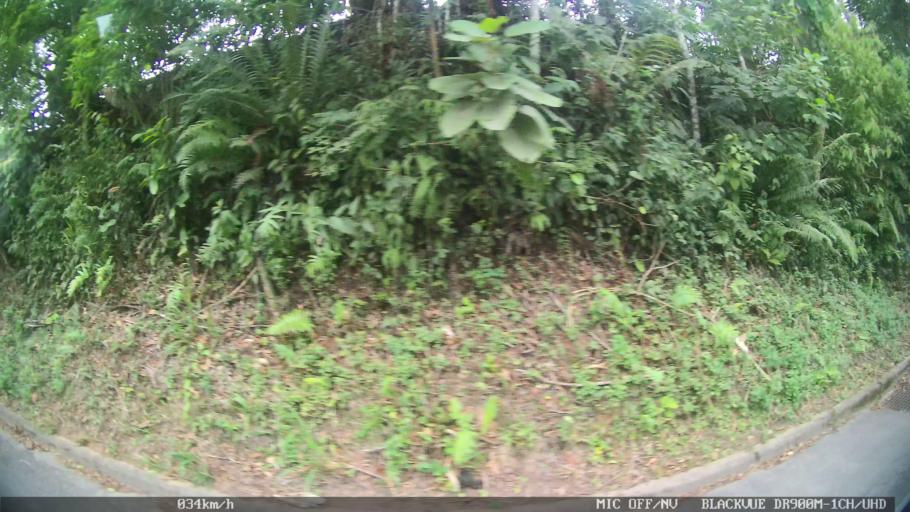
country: BR
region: Santa Catarina
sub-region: Joinville
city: Joinville
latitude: -26.2164
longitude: -48.9140
